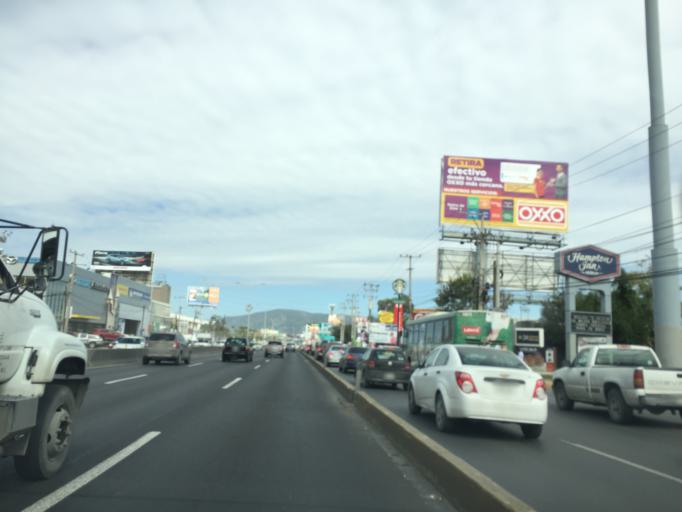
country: MX
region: Nuevo Leon
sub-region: Monterrey
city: Monterrey
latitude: 25.6776
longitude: -100.3522
